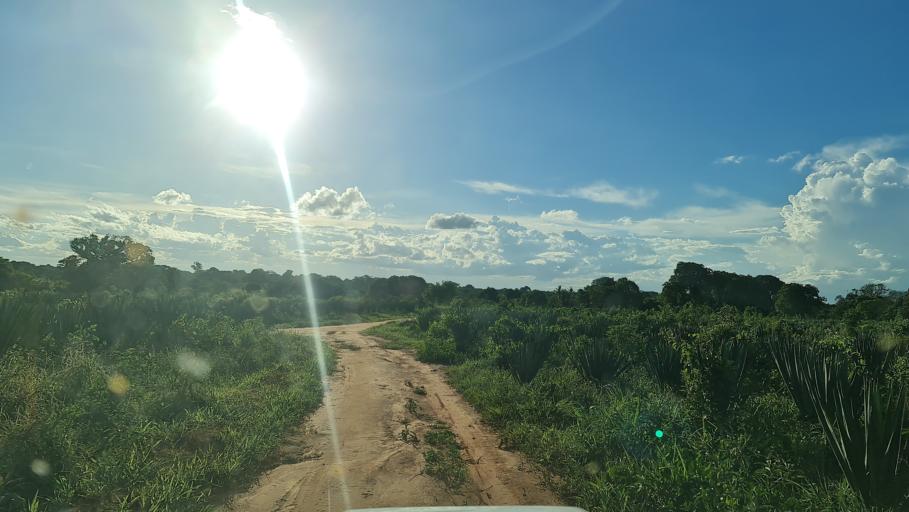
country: MZ
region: Nampula
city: Ilha de Mocambique
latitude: -14.9515
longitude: 40.1711
